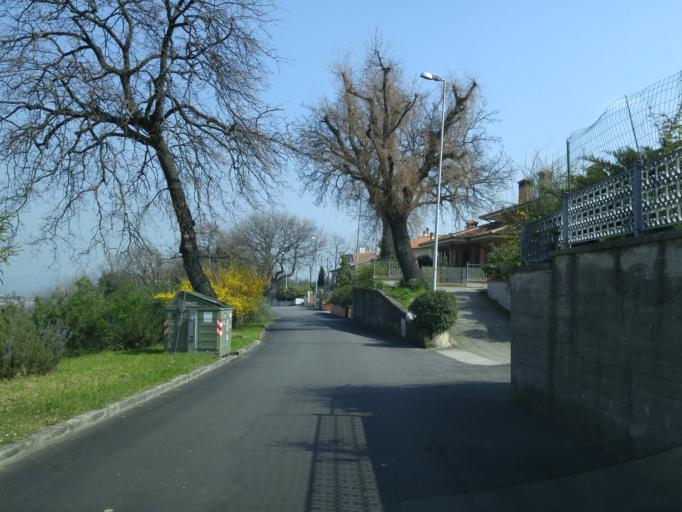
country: IT
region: The Marches
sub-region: Provincia di Pesaro e Urbino
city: Saltara
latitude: 43.7504
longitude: 12.8974
